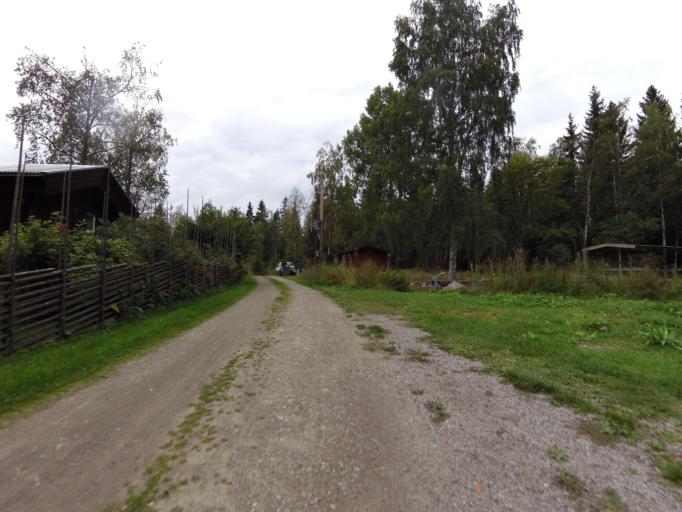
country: SE
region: Gaevleborg
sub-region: Gavle Kommun
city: Valbo
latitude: 60.7548
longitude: 16.9696
